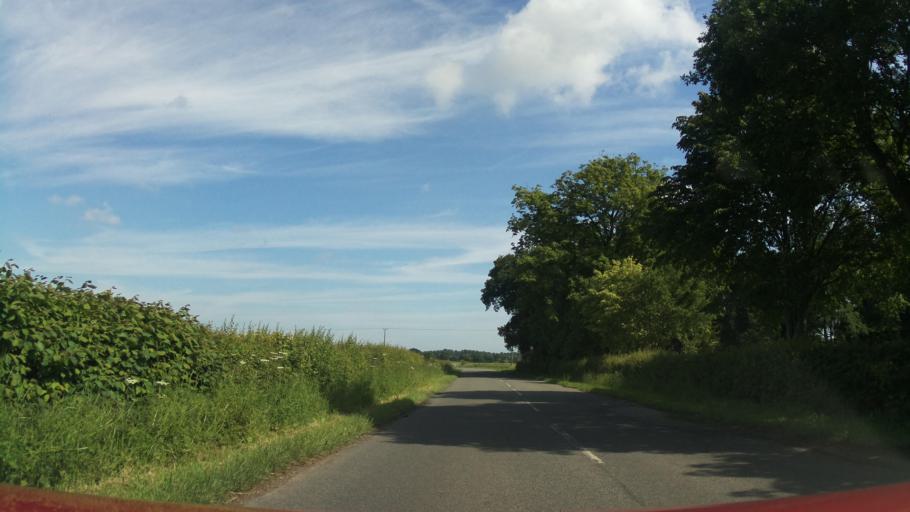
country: GB
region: England
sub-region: Lincolnshire
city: Skellingthorpe
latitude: 53.1383
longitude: -0.6327
